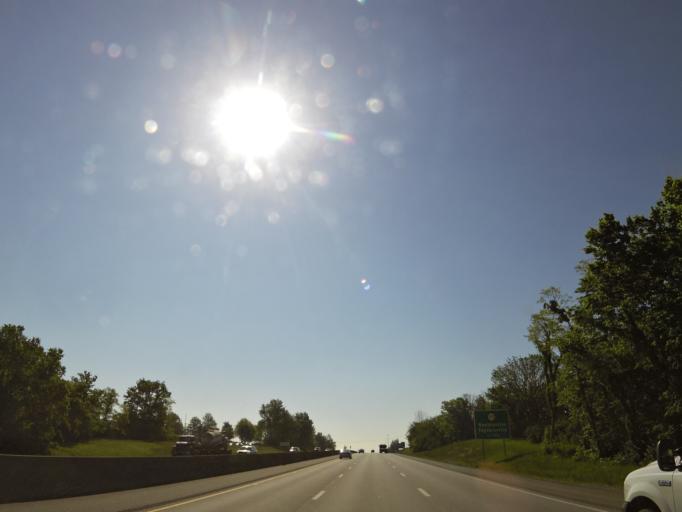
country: US
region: Kentucky
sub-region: Shelby County
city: Shelbyville
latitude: 38.1967
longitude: -85.2875
